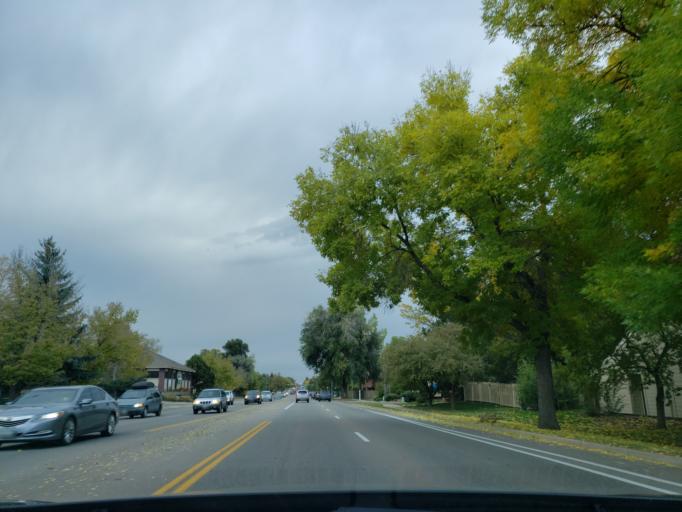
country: US
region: Colorado
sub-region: Larimer County
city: Fort Collins
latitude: 40.5604
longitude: -105.0960
